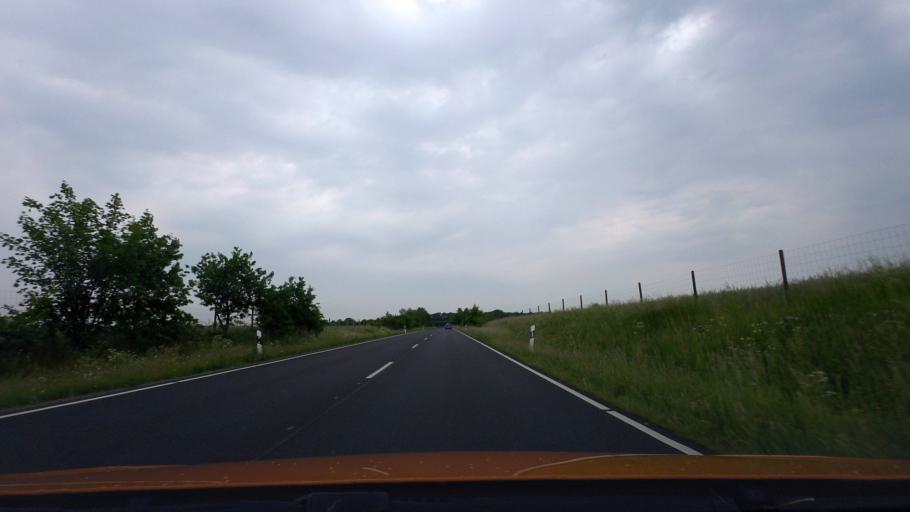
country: DE
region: Lower Saxony
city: Wietzen
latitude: 52.6692
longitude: 9.1043
